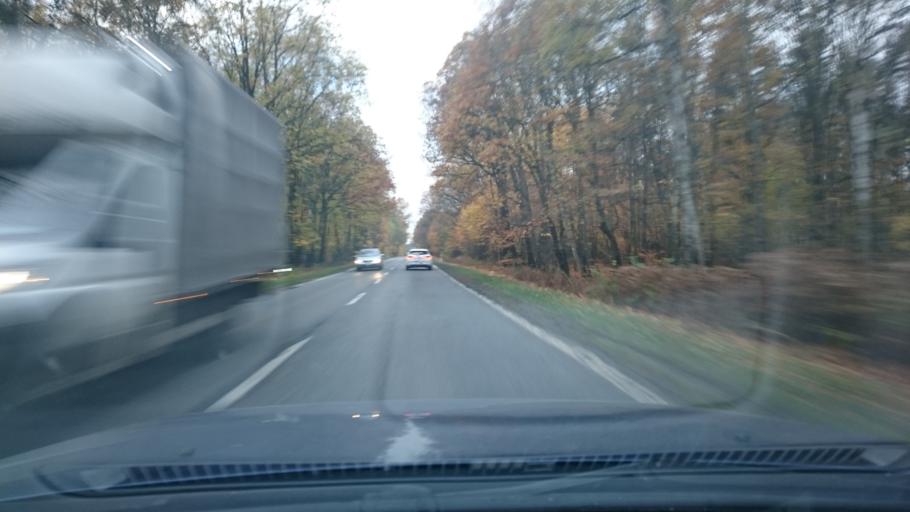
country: PL
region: Silesian Voivodeship
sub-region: Powiat rybnicki
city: Ksiazenice
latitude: 50.1182
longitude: 18.6033
